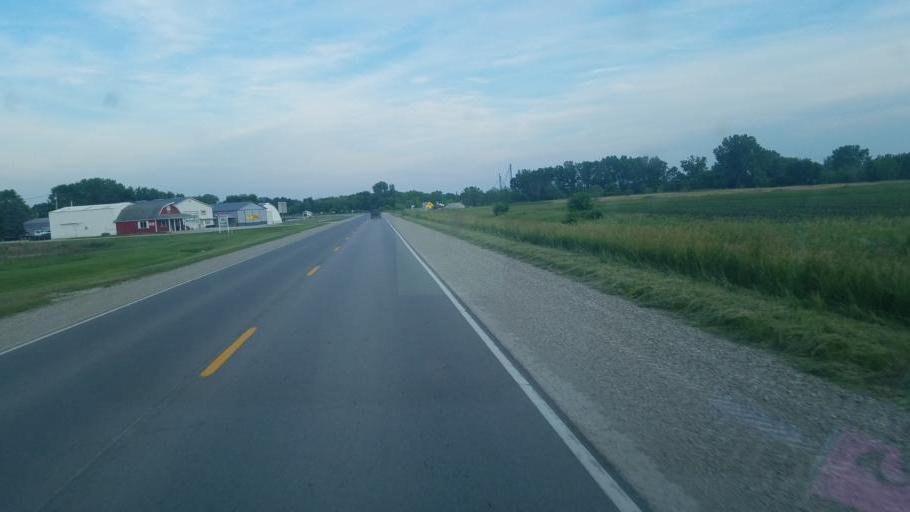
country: US
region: Iowa
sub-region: Benton County
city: Belle Plaine
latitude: 41.9005
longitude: -92.2915
